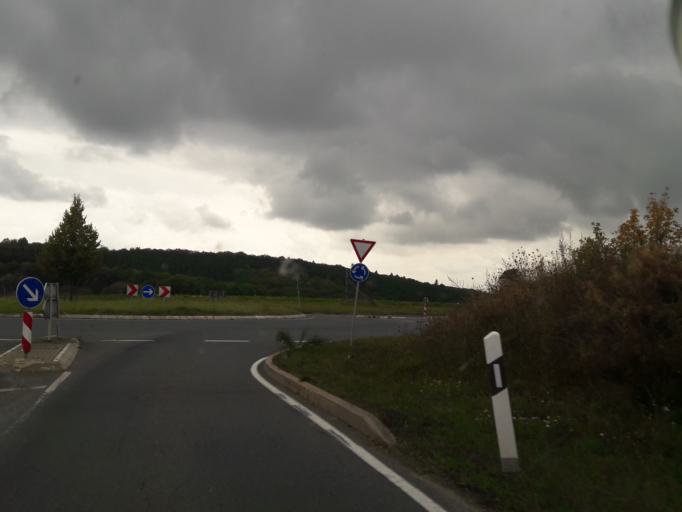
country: DE
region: Baden-Wuerttemberg
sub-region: Regierungsbezirk Stuttgart
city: Mockmuhl
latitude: 49.2947
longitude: 9.3687
